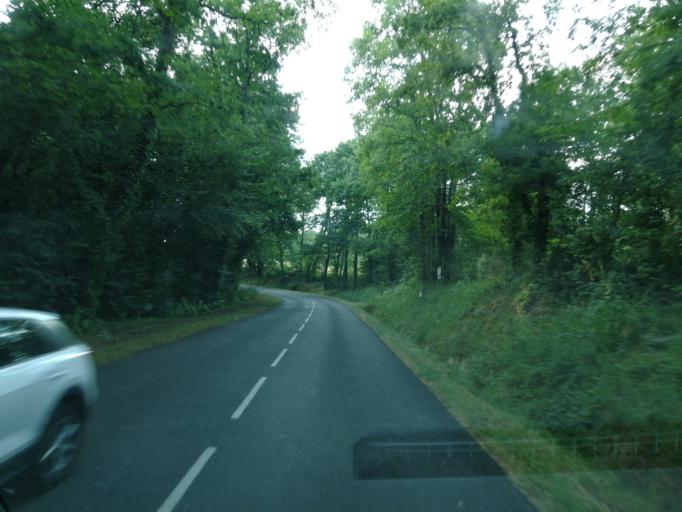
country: FR
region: Aquitaine
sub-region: Departement du Lot-et-Garonne
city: Monsempron-Libos
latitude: 44.5300
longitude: 0.9329
